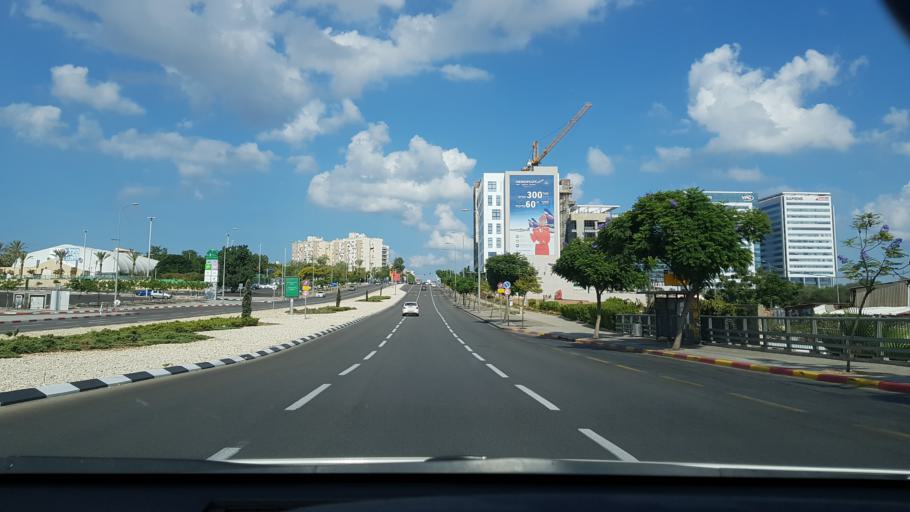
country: IL
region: Tel Aviv
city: Azor
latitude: 32.0030
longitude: 34.8020
